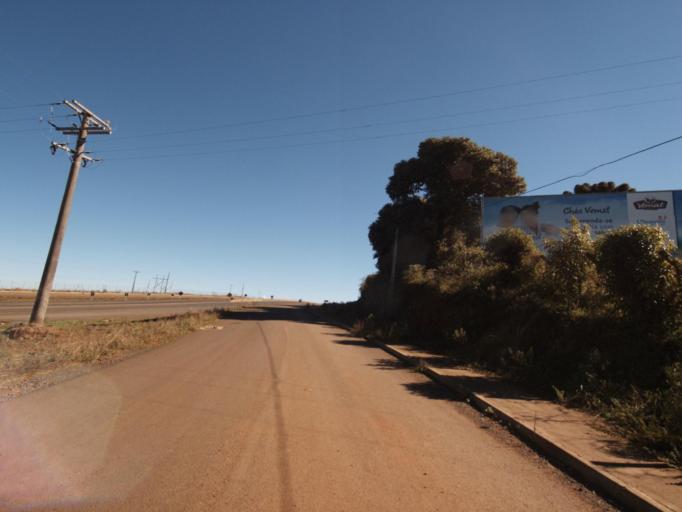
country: BR
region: Santa Catarina
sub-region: Xanxere
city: Xanxere
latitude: -26.8809
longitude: -52.3708
